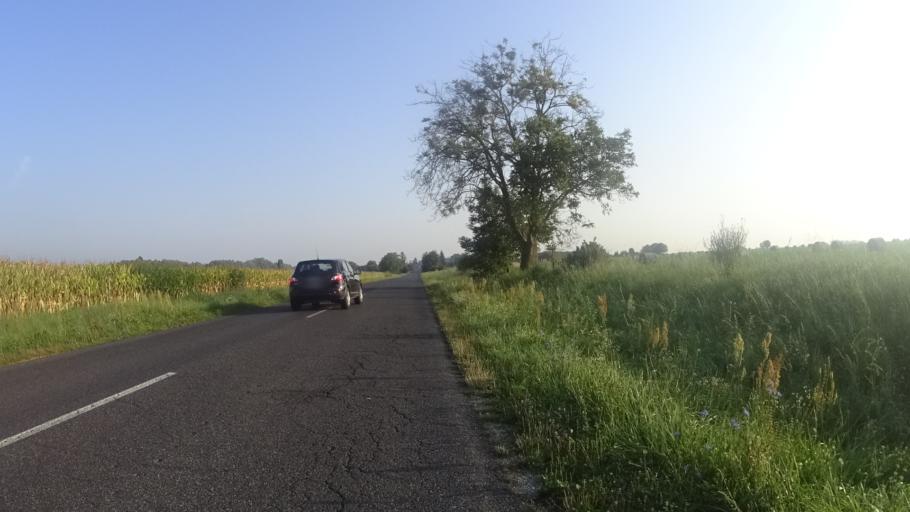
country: HU
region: Zala
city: Zalakomar
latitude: 46.5828
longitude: 17.1771
